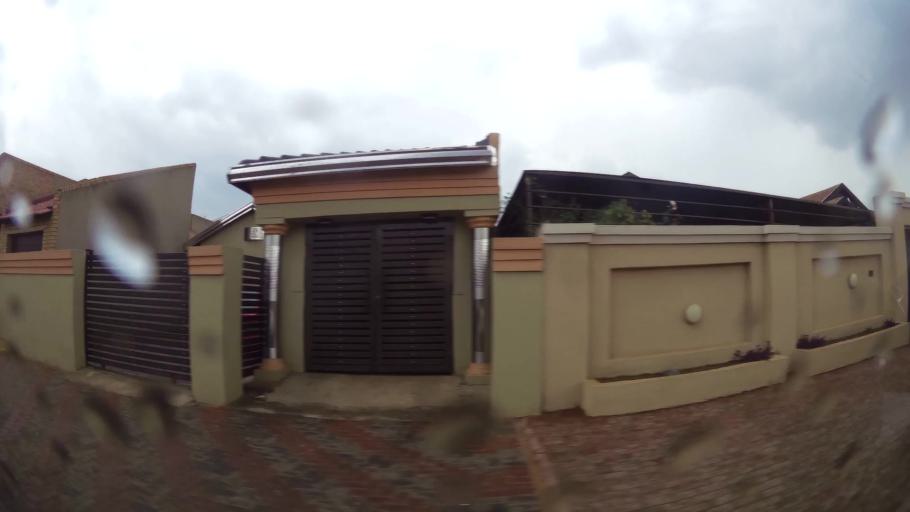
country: ZA
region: Gauteng
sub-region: Ekurhuleni Metropolitan Municipality
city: Germiston
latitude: -26.3667
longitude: 28.1641
